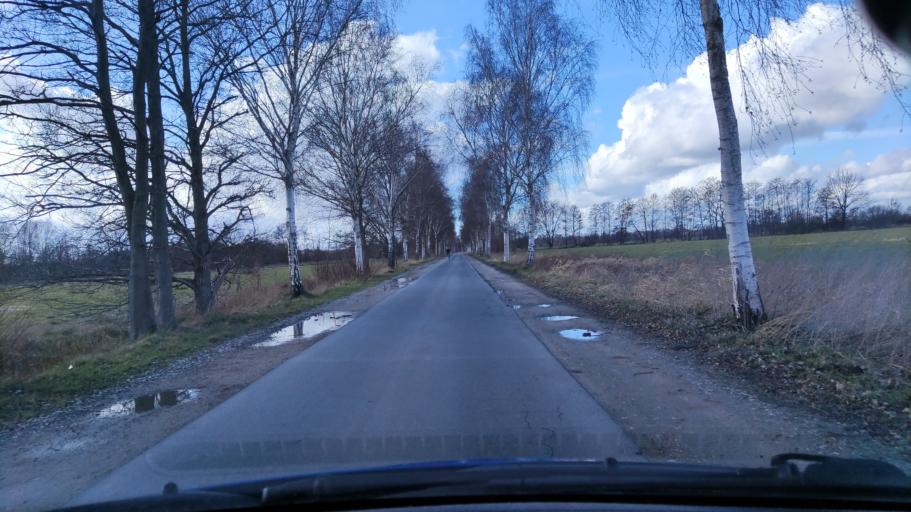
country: DE
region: Lower Saxony
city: Winsen
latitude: 53.3491
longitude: 10.1719
